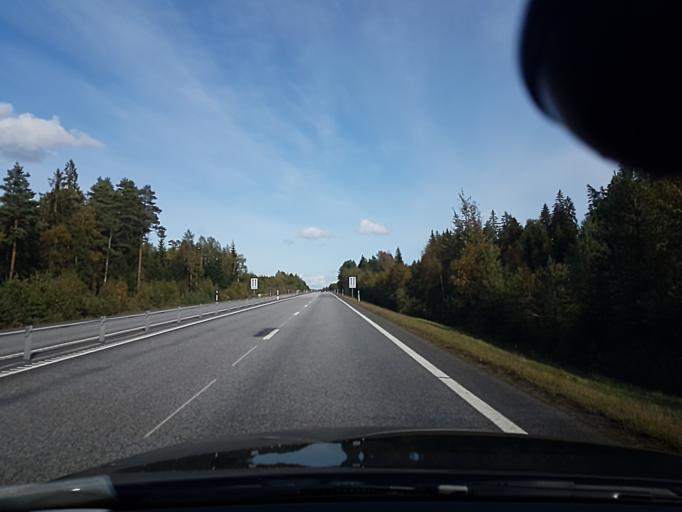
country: SE
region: Joenkoeping
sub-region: Varnamo Kommun
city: Forsheda
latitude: 57.1698
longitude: 13.8964
